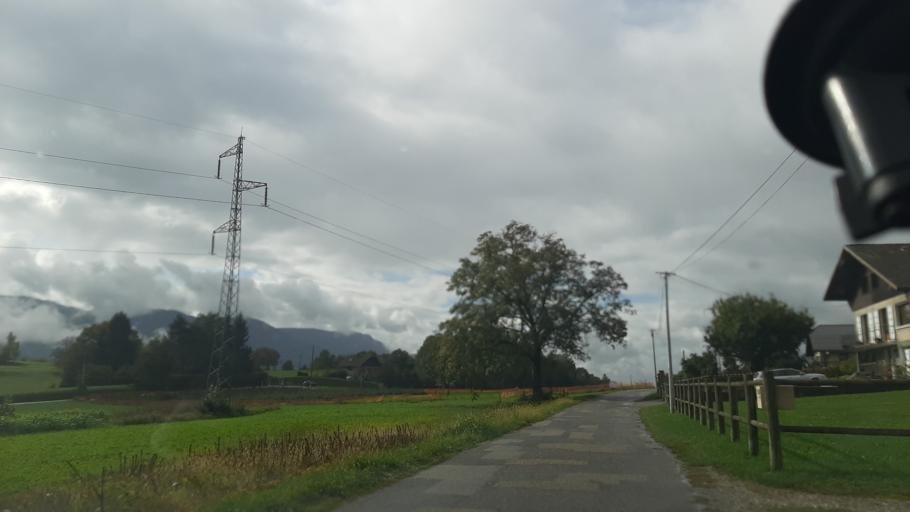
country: FR
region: Rhone-Alpes
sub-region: Departement de la Savoie
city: Gresy-sur-Isere
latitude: 45.6092
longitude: 6.2654
